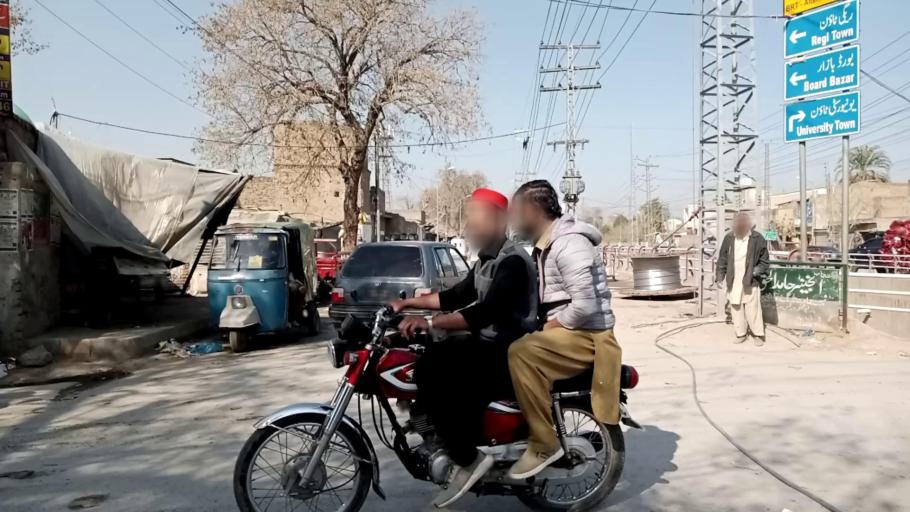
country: PK
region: Khyber Pakhtunkhwa
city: Peshawar
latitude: 33.9908
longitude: 71.4858
